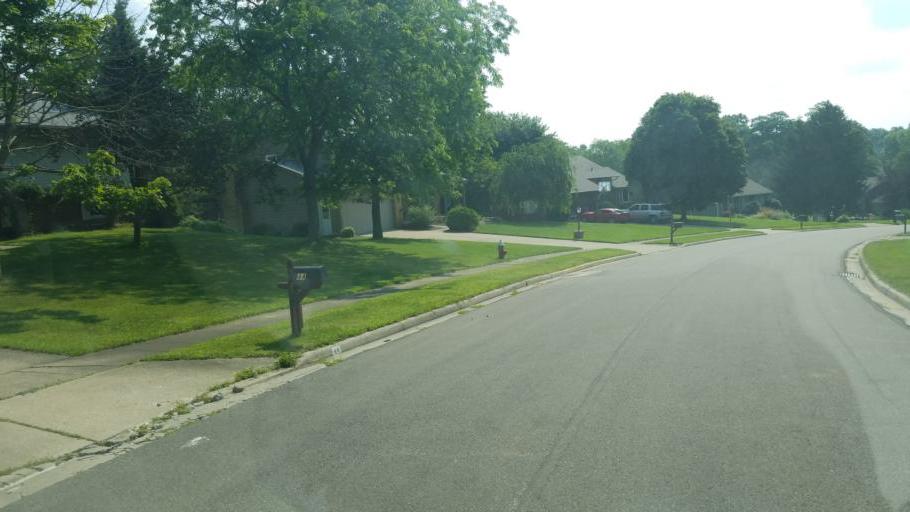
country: US
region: Ohio
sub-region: Richland County
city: Lexington
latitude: 40.6832
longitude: -82.6037
